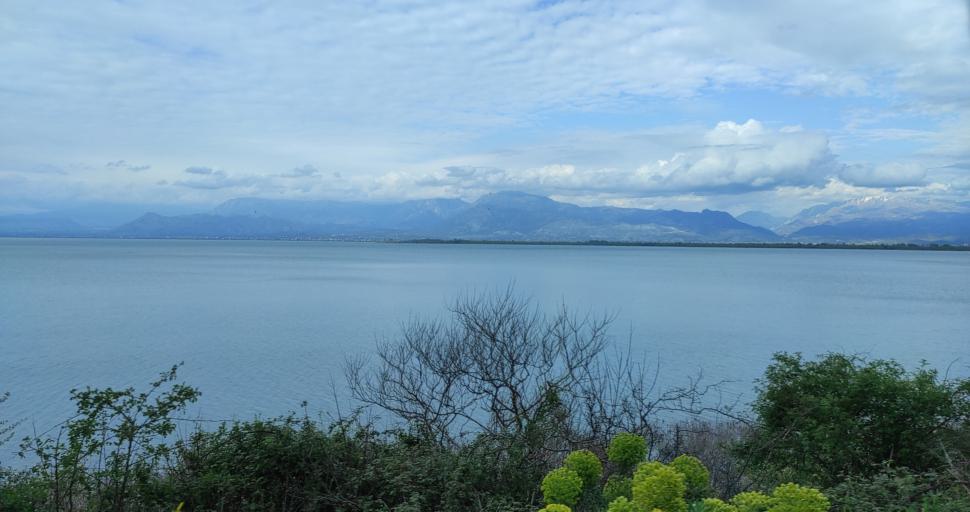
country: AL
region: Shkoder
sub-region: Rrethi i Shkodres
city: Berdica e Madhe
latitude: 42.0638
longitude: 19.4382
